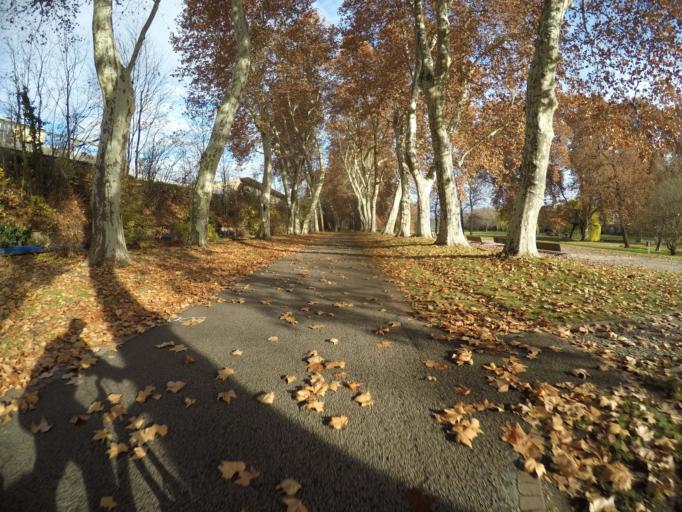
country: DE
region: Baden-Wuerttemberg
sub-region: Regierungsbezirk Stuttgart
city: Stuttgart-Ost
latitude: 48.7941
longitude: 9.1966
